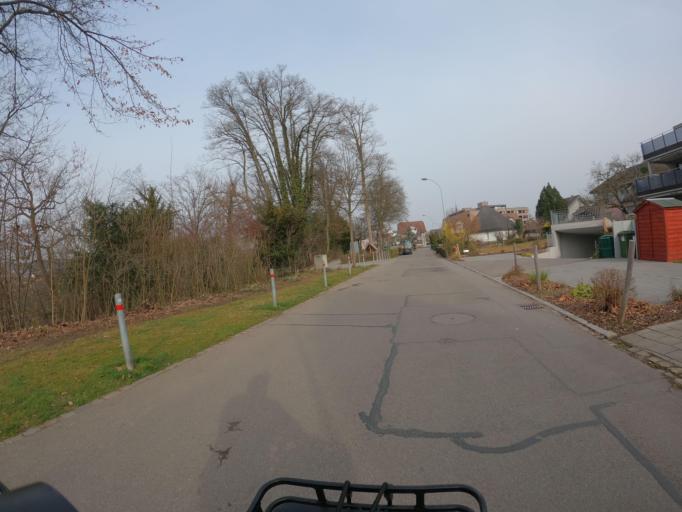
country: CH
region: Aargau
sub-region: Bezirk Bremgarten
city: Bremgarten
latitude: 47.3477
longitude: 8.3461
